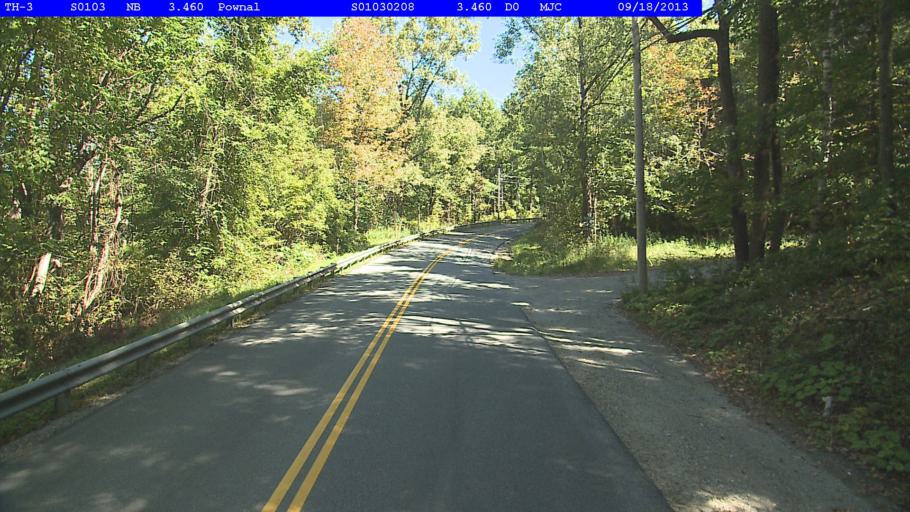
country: US
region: Vermont
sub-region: Bennington County
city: Bennington
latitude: 42.7962
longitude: -73.2120
